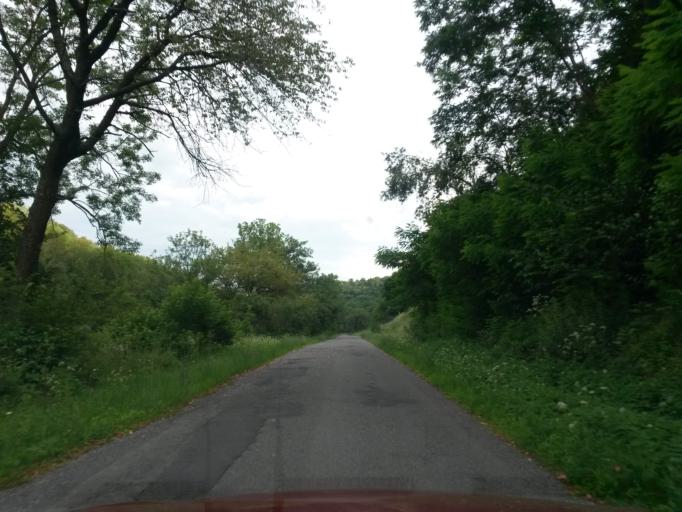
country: SK
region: Banskobystricky
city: Velky Krtis
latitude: 48.3118
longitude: 19.4592
